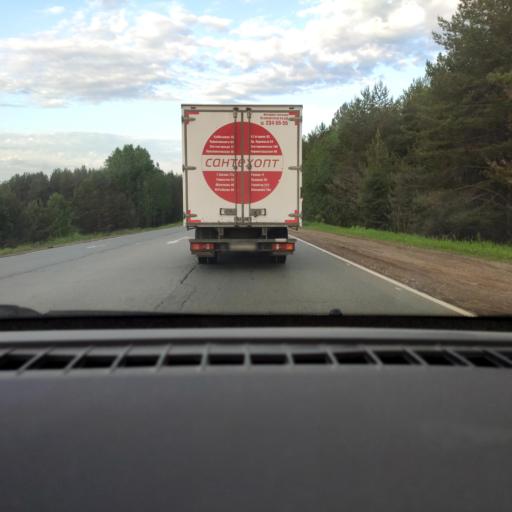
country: RU
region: Perm
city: Nytva
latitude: 57.9538
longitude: 55.1562
